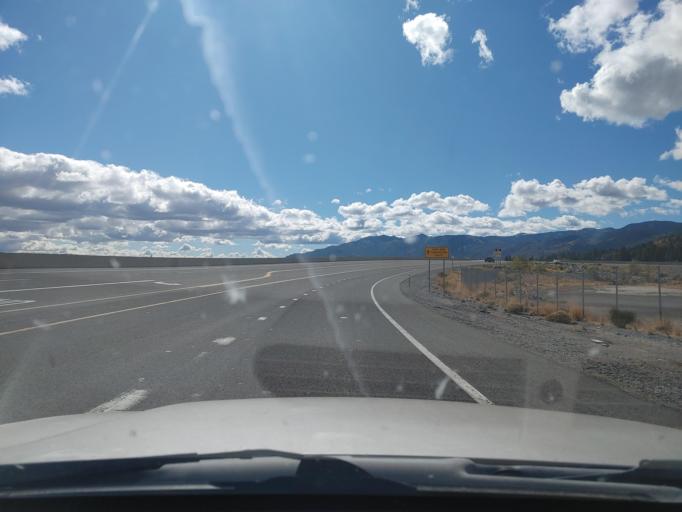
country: US
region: Nevada
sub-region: Carson City
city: Carson City
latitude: 39.3084
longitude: -119.8240
